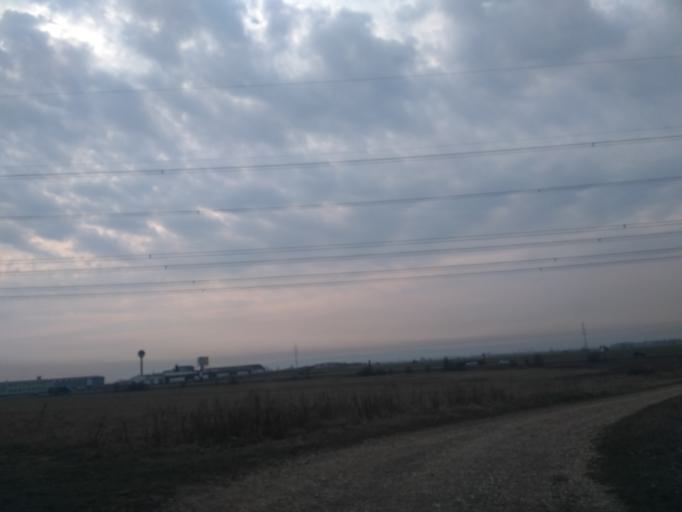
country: SK
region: Kosicky
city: Moldava nad Bodvou
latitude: 48.6085
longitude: 21.1071
